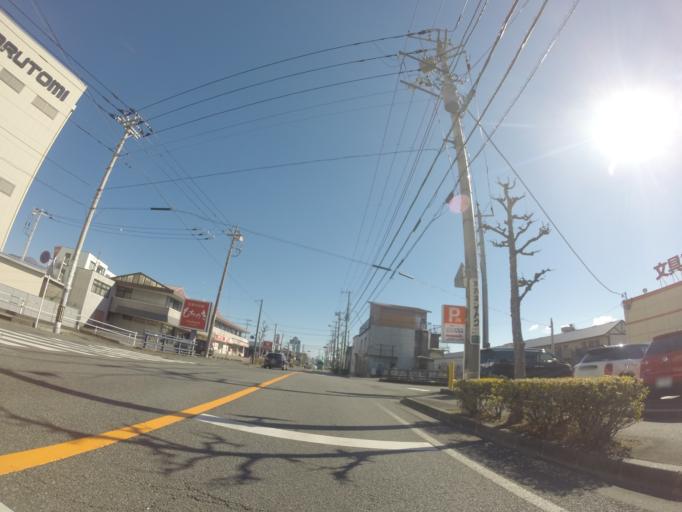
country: JP
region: Shizuoka
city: Fuji
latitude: 35.1622
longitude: 138.6944
